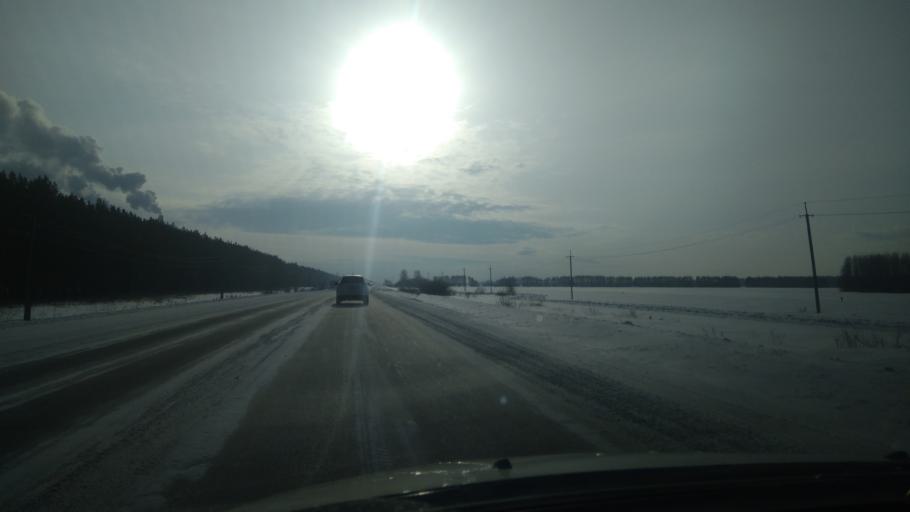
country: RU
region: Sverdlovsk
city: Sukhoy Log
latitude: 56.8770
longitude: 62.0454
